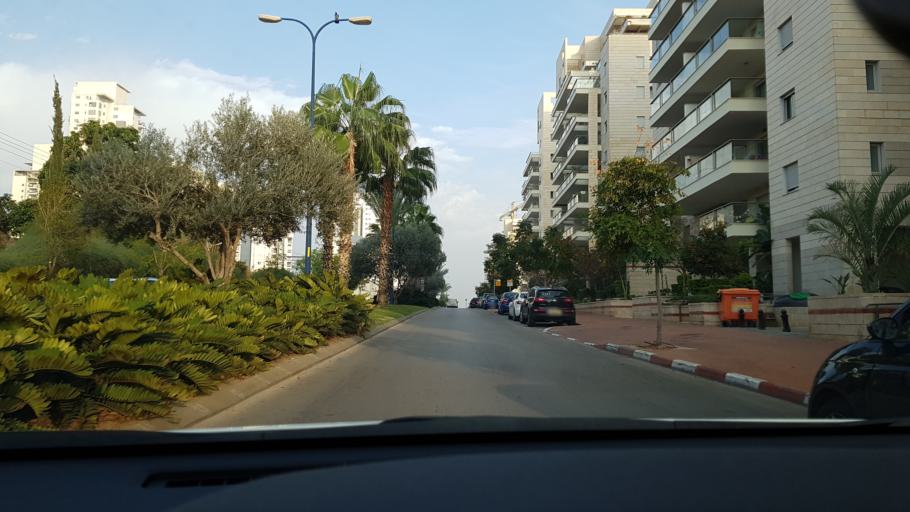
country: IL
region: Central District
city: Ness Ziona
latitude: 31.9049
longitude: 34.8190
